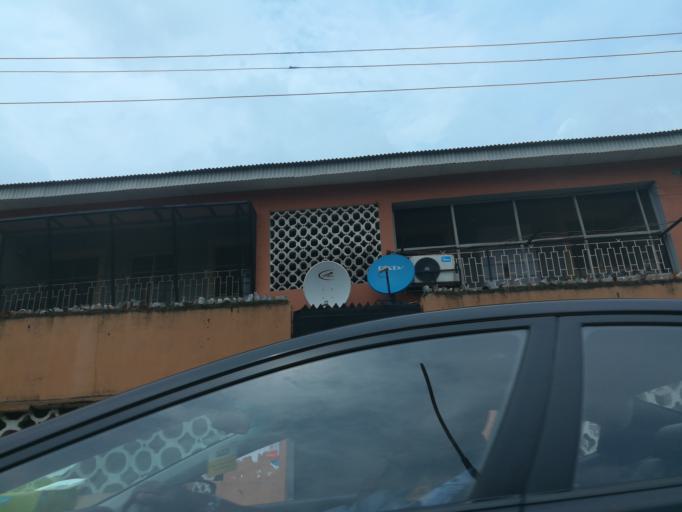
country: NG
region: Lagos
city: Ojota
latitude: 6.5684
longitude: 3.3653
